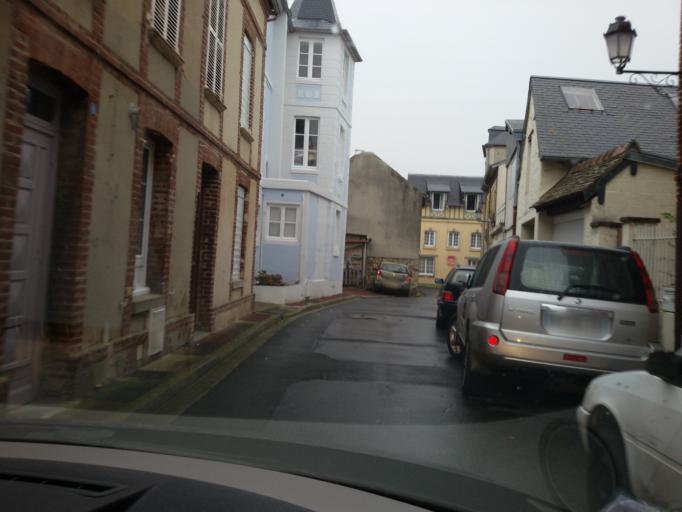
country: FR
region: Lower Normandy
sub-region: Departement du Calvados
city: Trouville-sur-Mer
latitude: 49.4004
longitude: 0.1275
